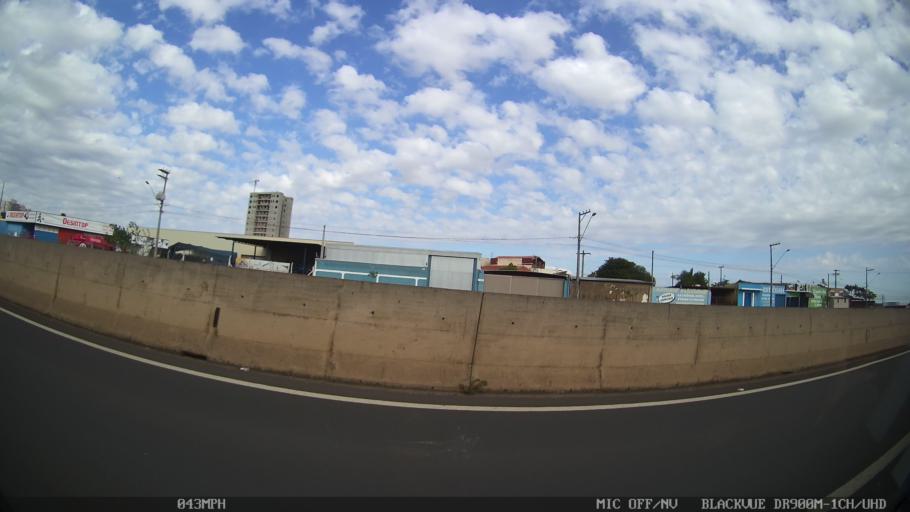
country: BR
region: Sao Paulo
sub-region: Limeira
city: Limeira
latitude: -22.5636
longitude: -47.4259
